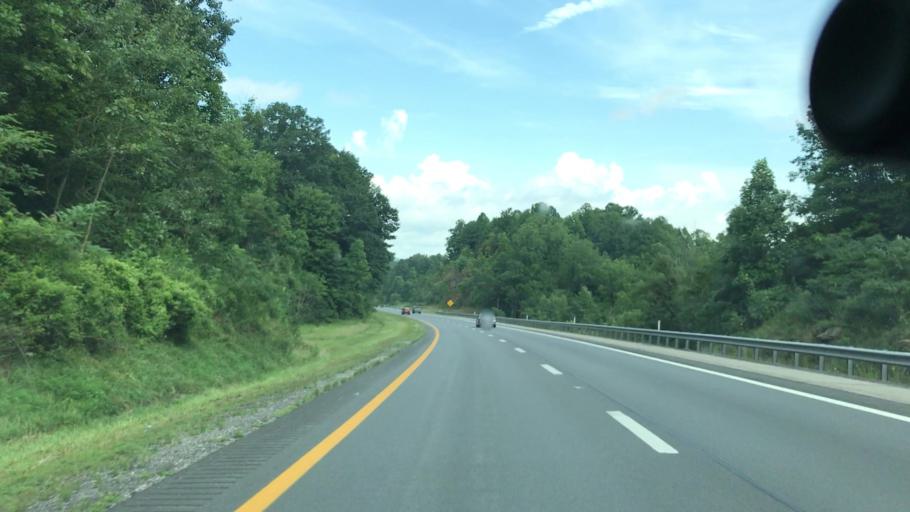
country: US
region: West Virginia
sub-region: Raleigh County
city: Bradley
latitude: 37.8909
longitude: -81.2656
